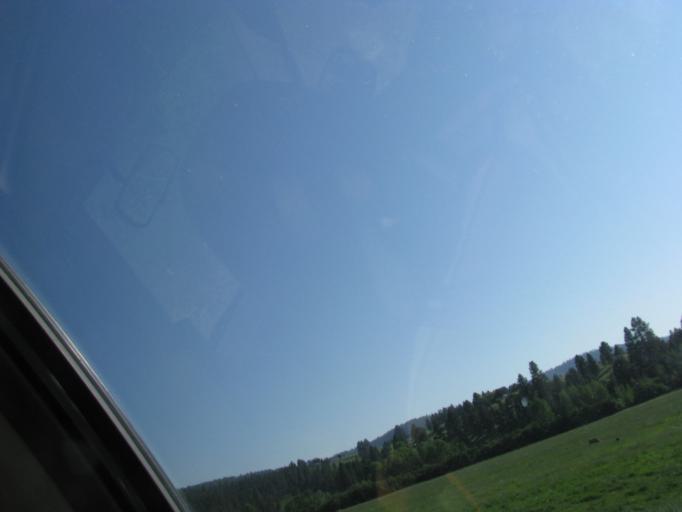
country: US
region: Washington
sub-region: Spokane County
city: Liberty Lake
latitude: 47.6178
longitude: -117.1106
